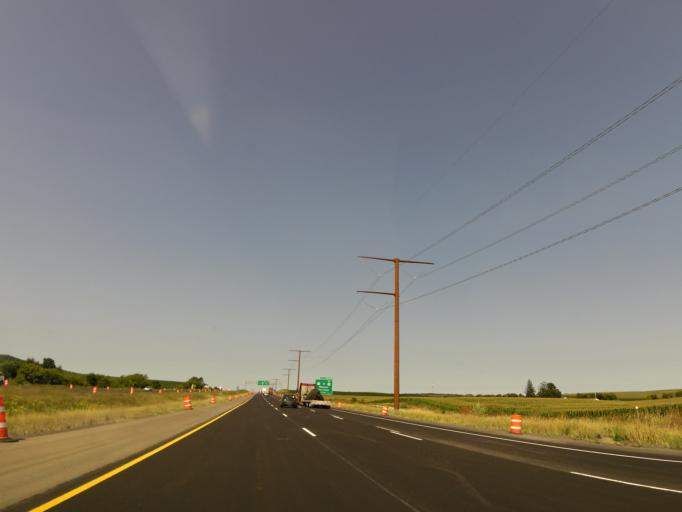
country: US
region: Wisconsin
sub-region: Columbia County
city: Portage
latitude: 43.4648
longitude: -89.4961
